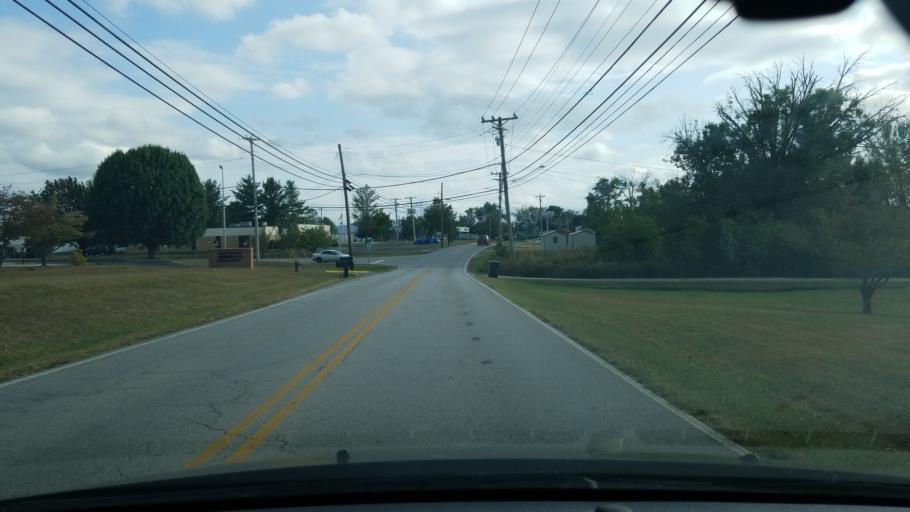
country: US
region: Tennessee
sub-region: Cumberland County
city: Crossville
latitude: 35.9686
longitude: -85.0363
